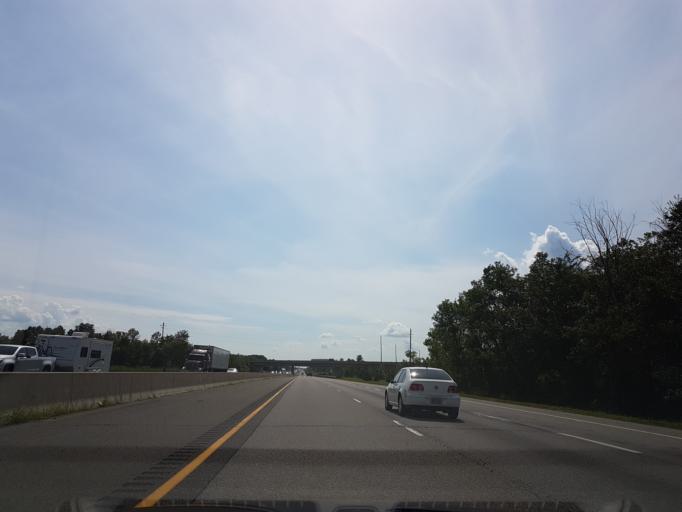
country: CA
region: Ontario
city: Prescott
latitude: 44.7501
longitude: -75.4850
